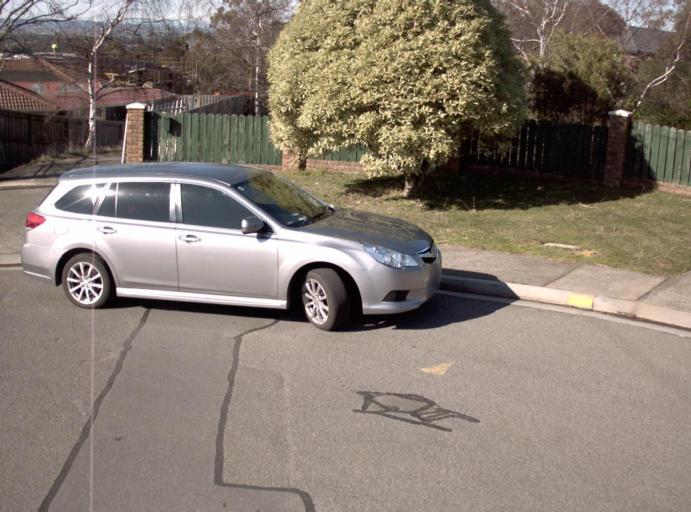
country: AU
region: Tasmania
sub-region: Launceston
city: Summerhill
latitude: -41.4724
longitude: 147.1517
